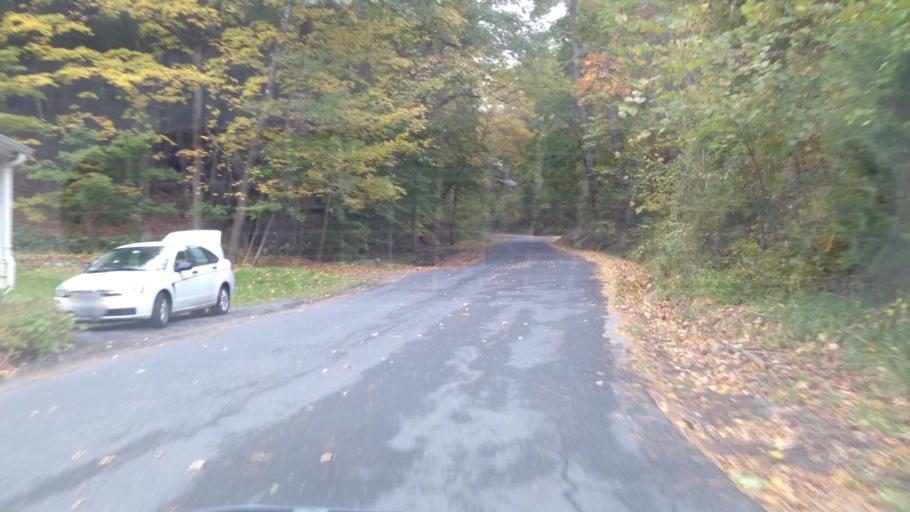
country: US
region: New York
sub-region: Ulster County
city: Rosendale Village
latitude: 41.8416
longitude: -74.0838
